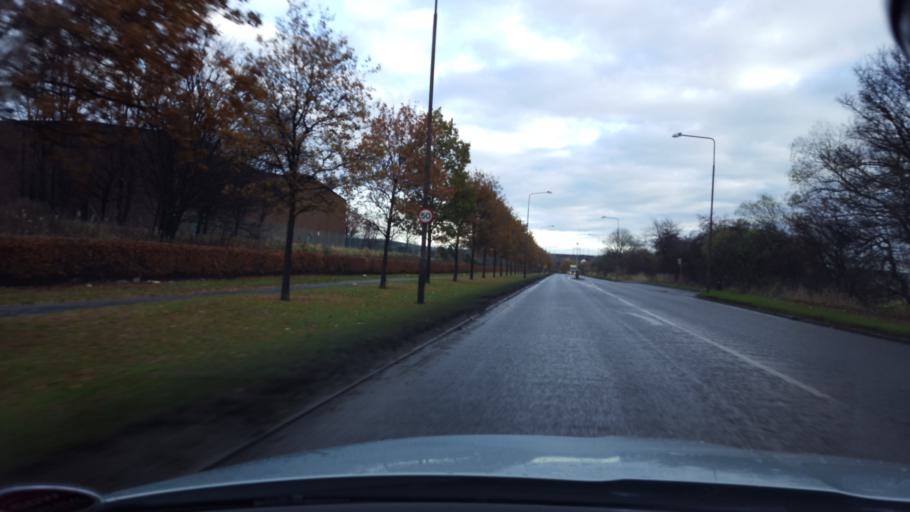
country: GB
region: Scotland
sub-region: West Lothian
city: Broxburn
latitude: 55.9356
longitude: -3.4431
